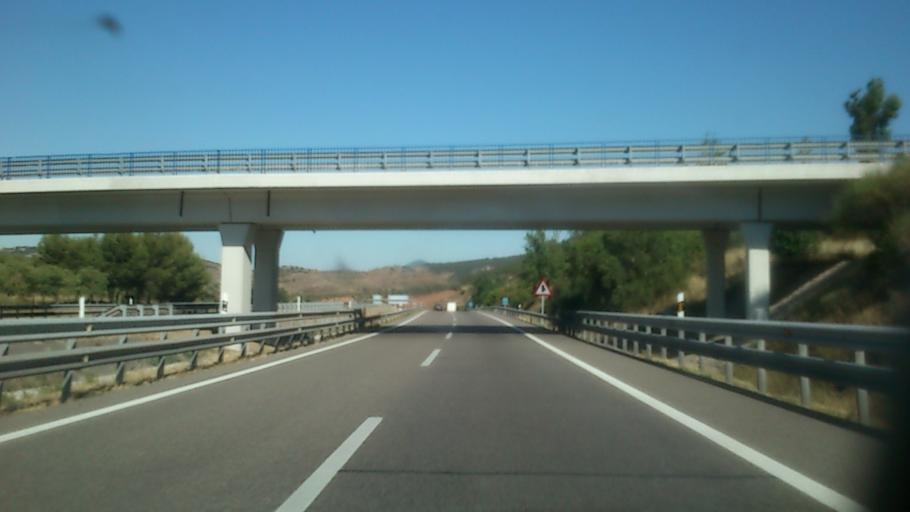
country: ES
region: Aragon
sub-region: Provincia de Zaragoza
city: Paracuellos de la Ribera
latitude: 41.4134
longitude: -1.5187
